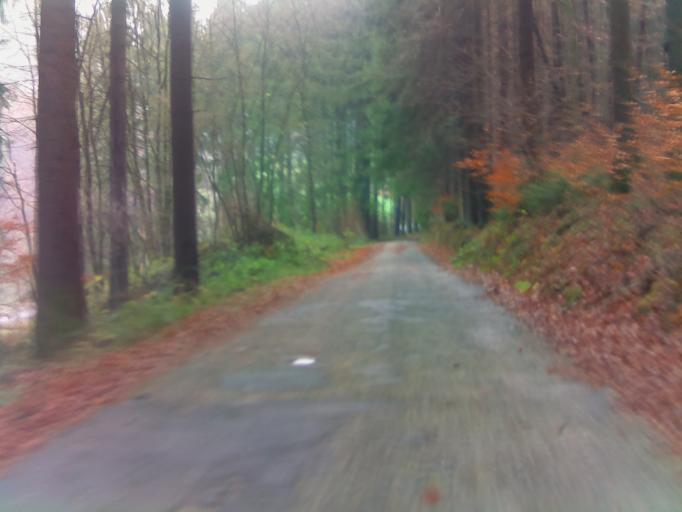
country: DE
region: Baden-Wuerttemberg
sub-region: Karlsruhe Region
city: Heddesbach
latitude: 49.4909
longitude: 8.8389
